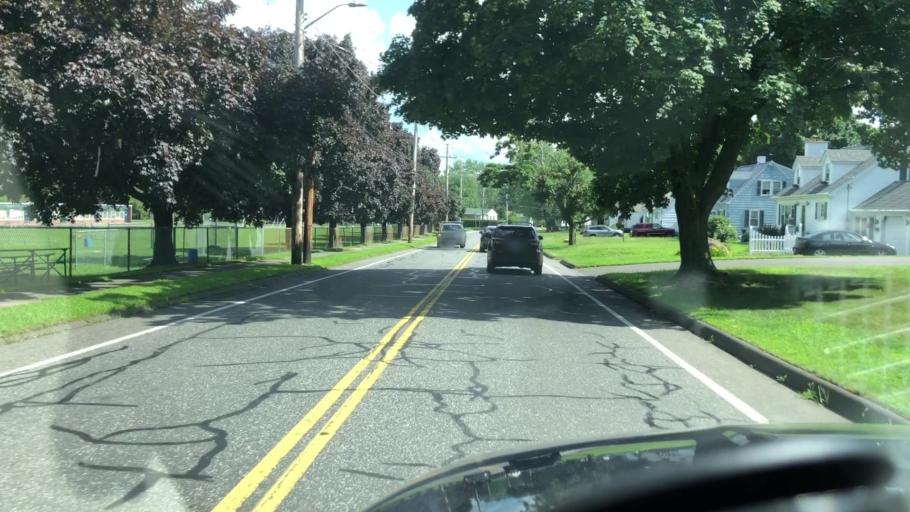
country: US
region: Massachusetts
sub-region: Hampden County
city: Holyoke
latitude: 42.1849
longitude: -72.6499
